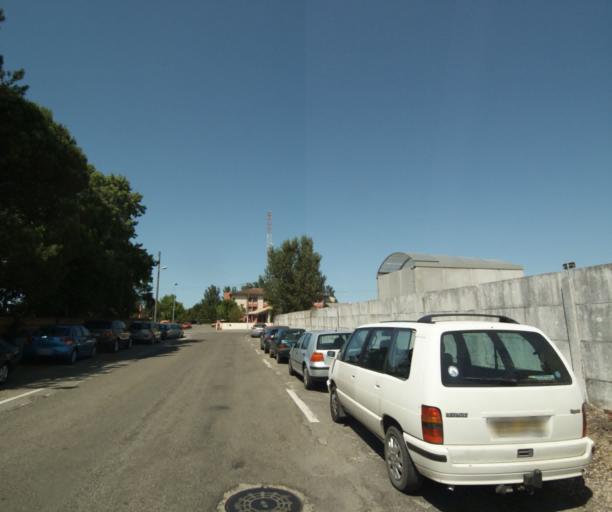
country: FR
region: Midi-Pyrenees
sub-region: Departement du Tarn-et-Garonne
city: Montauban
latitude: 44.0402
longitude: 1.3648
